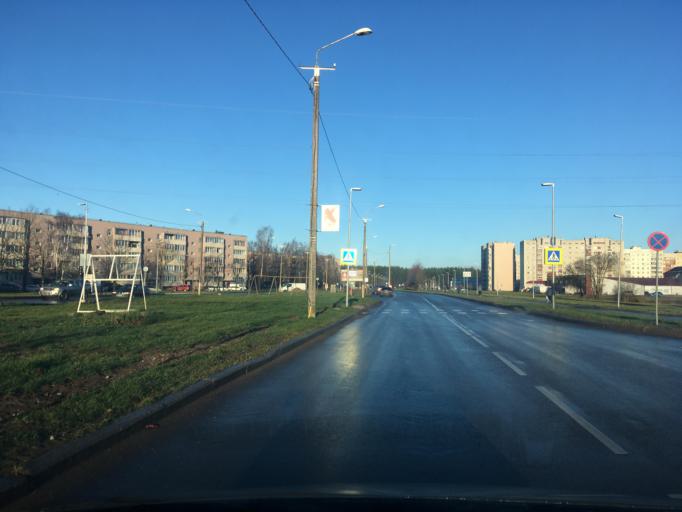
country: EE
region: Ida-Virumaa
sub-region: Narva linn
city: Narva
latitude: 59.3869
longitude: 28.1760
